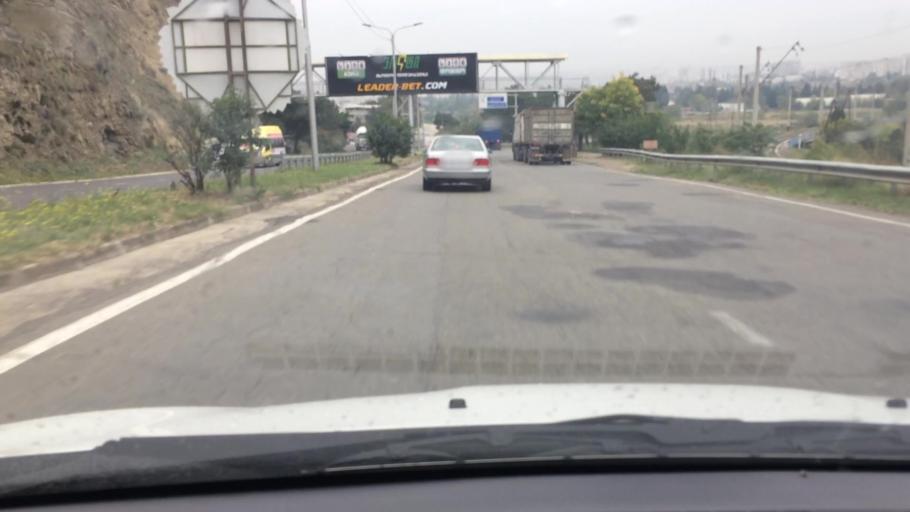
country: GE
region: T'bilisi
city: Tbilisi
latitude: 41.6586
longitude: 44.8904
